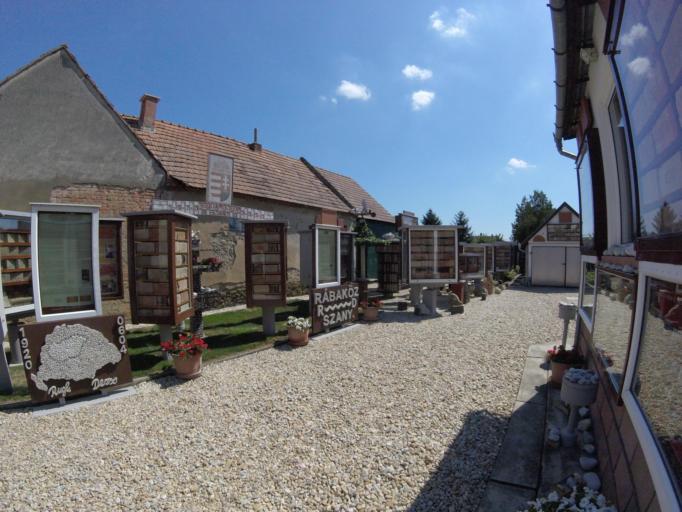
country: HU
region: Gyor-Moson-Sopron
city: Szany
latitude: 47.4545
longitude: 17.3123
